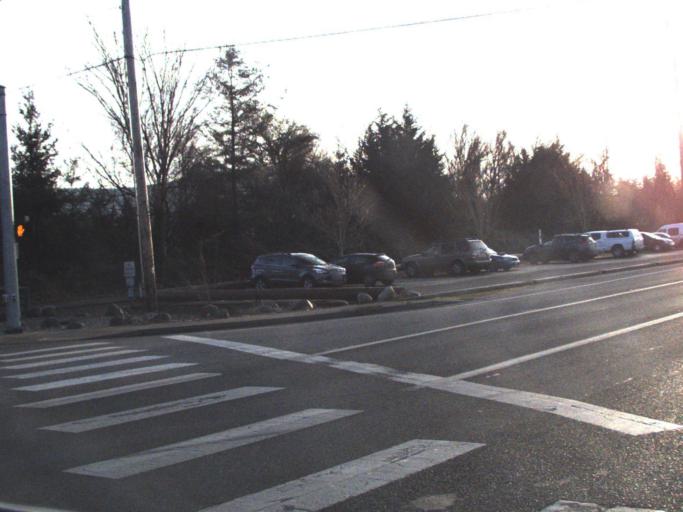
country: US
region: Washington
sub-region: Skagit County
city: Sedro-Woolley
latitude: 48.5158
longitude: -122.2108
